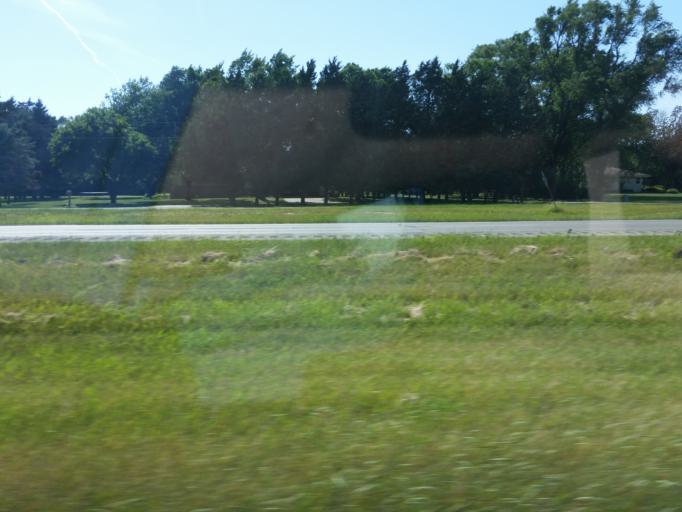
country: US
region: Illinois
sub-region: Winnebago County
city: Roscoe
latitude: 42.4015
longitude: -89.0113
